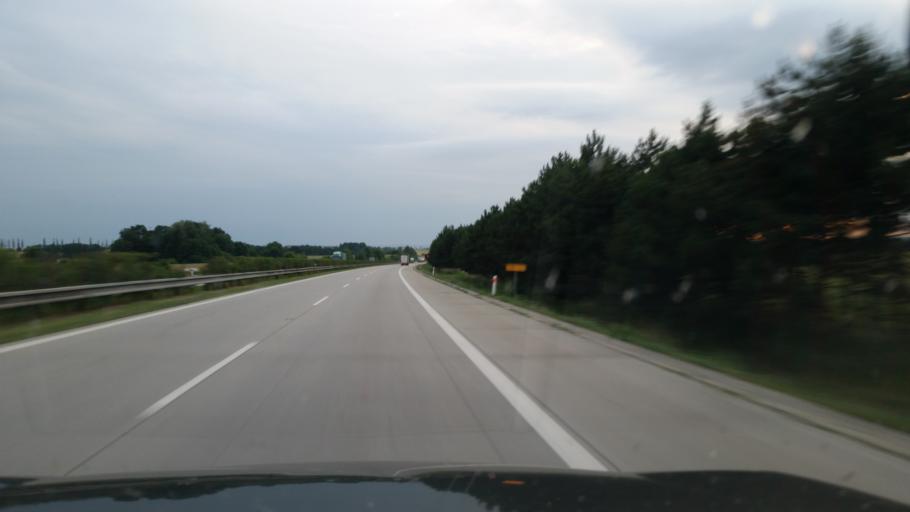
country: CZ
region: Olomoucky
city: Doloplazy
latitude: 49.5837
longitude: 17.4366
